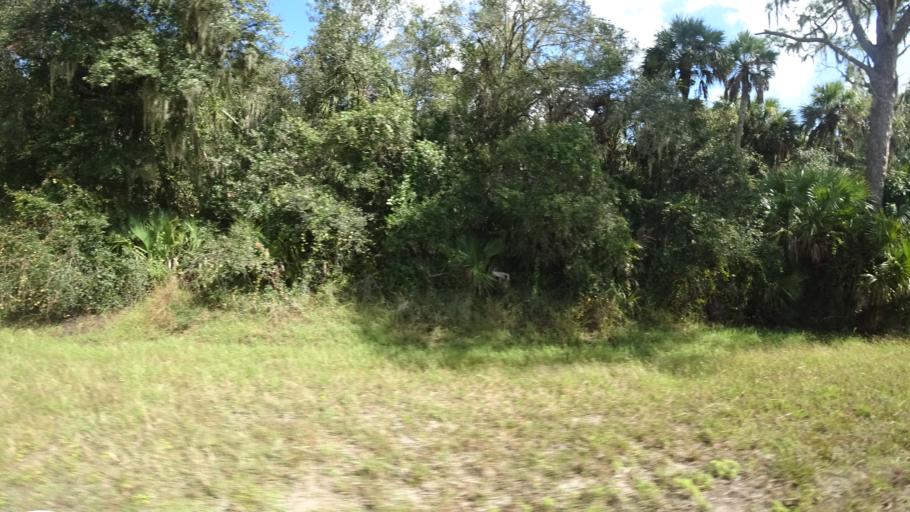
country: US
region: Florida
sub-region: Sarasota County
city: North Port
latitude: 27.2228
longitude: -82.1220
